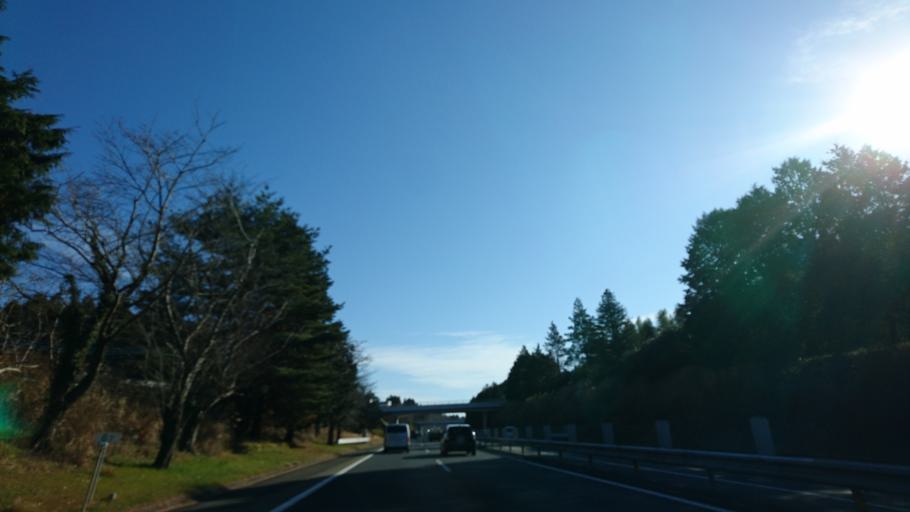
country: JP
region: Chiba
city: Yotsukaido
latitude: 35.5727
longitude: 140.2192
